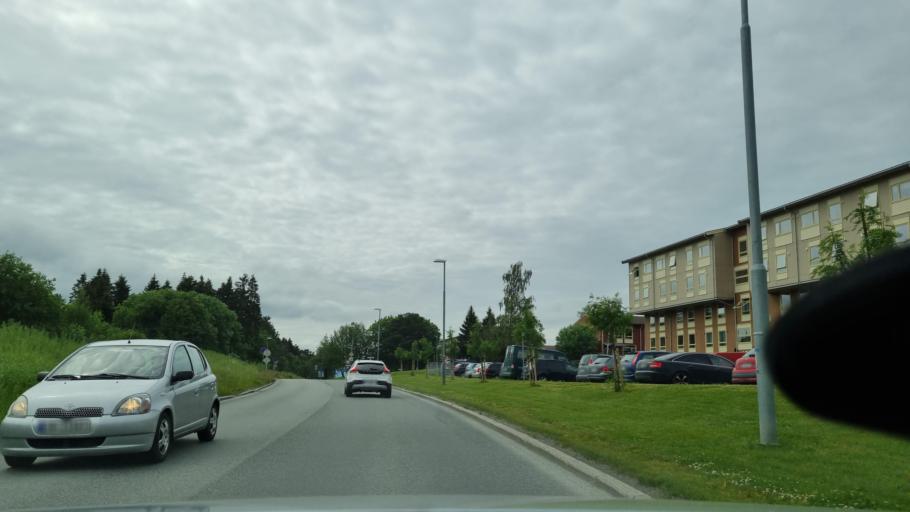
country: NO
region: Sor-Trondelag
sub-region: Melhus
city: Melhus
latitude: 63.3460
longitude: 10.3436
